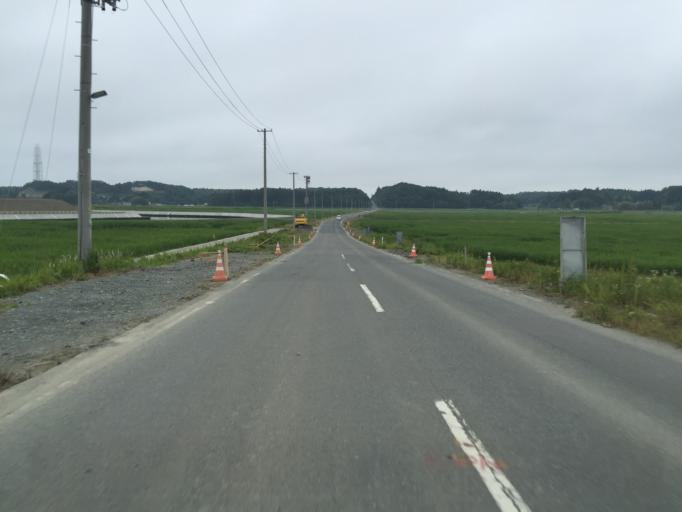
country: JP
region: Fukushima
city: Namie
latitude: 37.6862
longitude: 141.0051
